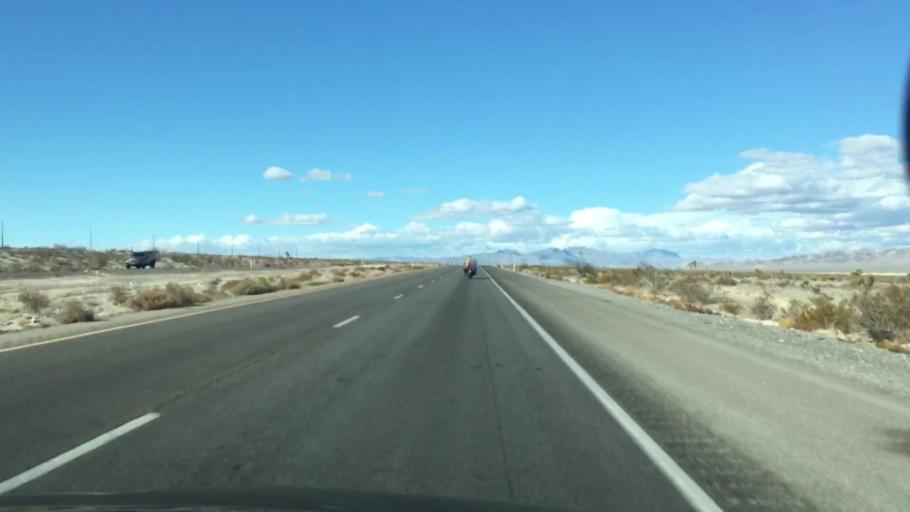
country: US
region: Nevada
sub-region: Clark County
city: Summerlin South
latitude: 36.4395
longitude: -115.4313
